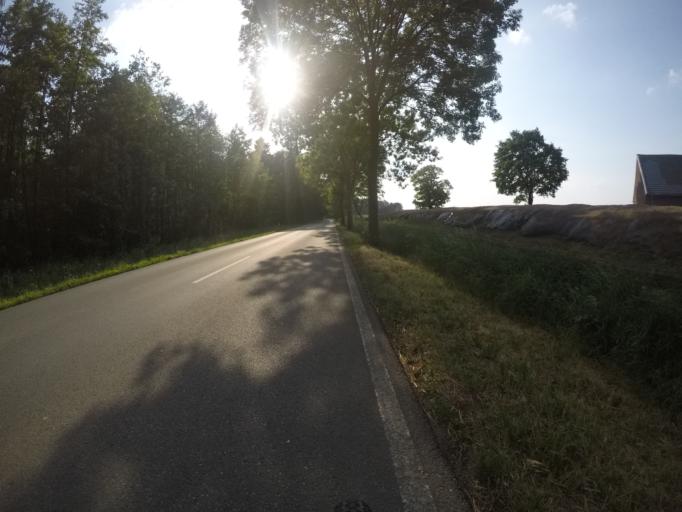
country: DE
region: North Rhine-Westphalia
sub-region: Regierungsbezirk Munster
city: Isselburg
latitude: 51.8427
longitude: 6.4966
